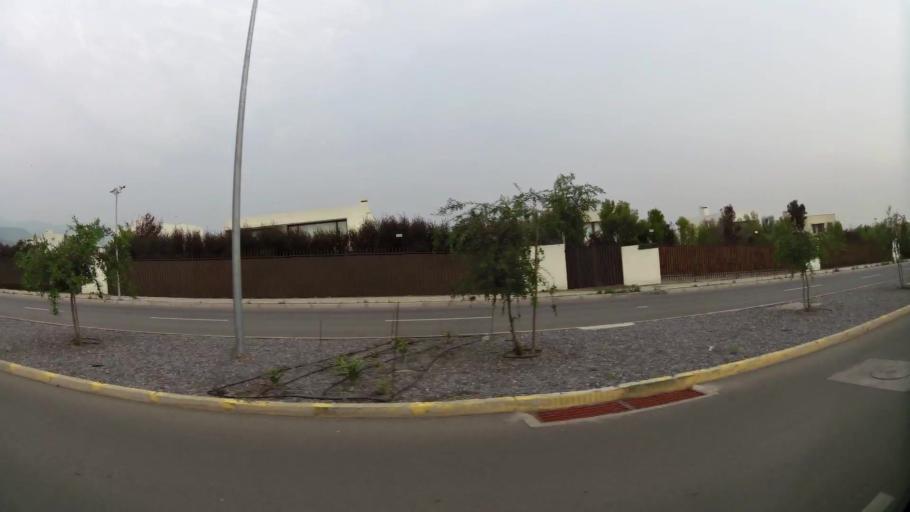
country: CL
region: Santiago Metropolitan
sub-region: Provincia de Chacabuco
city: Chicureo Abajo
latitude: -33.2573
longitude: -70.6243
